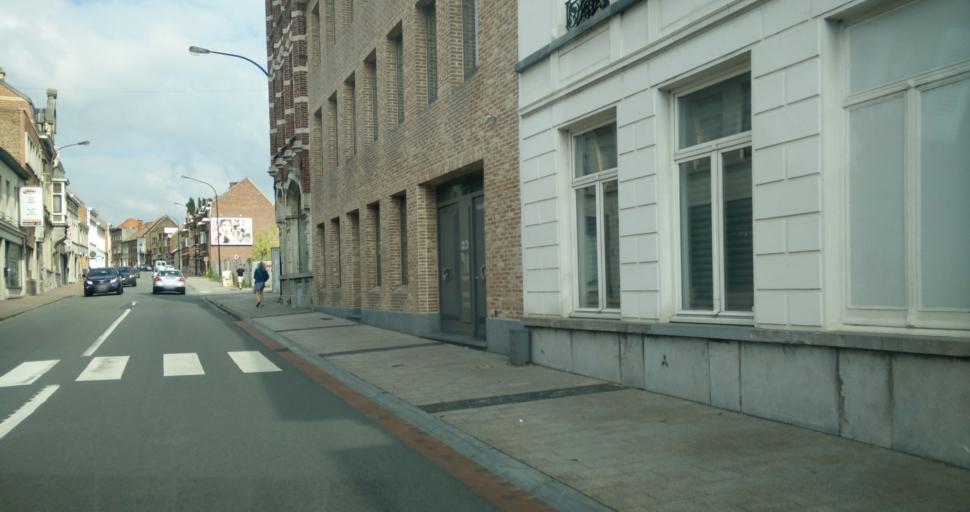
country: BE
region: Flanders
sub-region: Provincie Oost-Vlaanderen
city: Ronse
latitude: 50.7502
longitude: 3.5968
